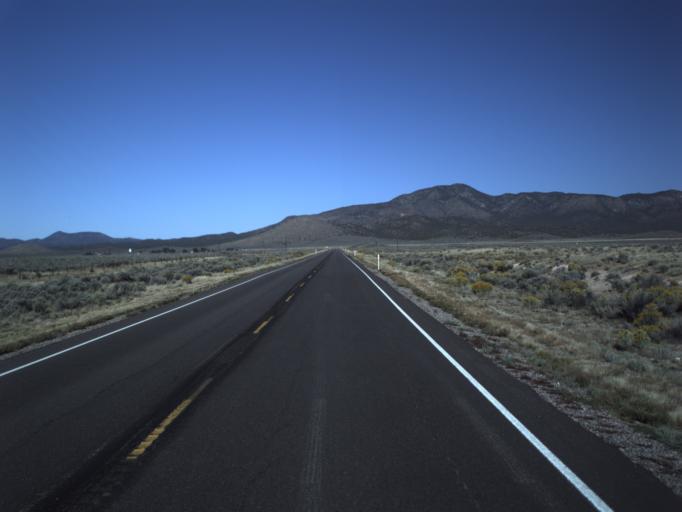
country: US
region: Utah
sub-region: Washington County
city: Enterprise
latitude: 37.7937
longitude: -113.8969
